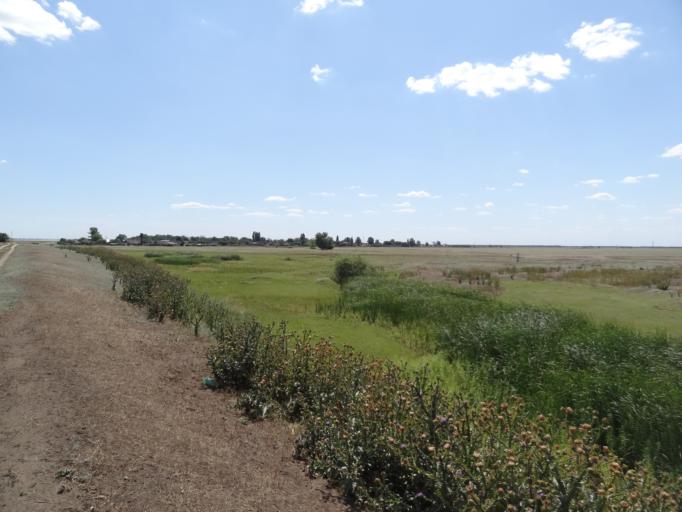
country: RU
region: Saratov
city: Sovetskoye
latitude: 51.2899
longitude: 46.6515
